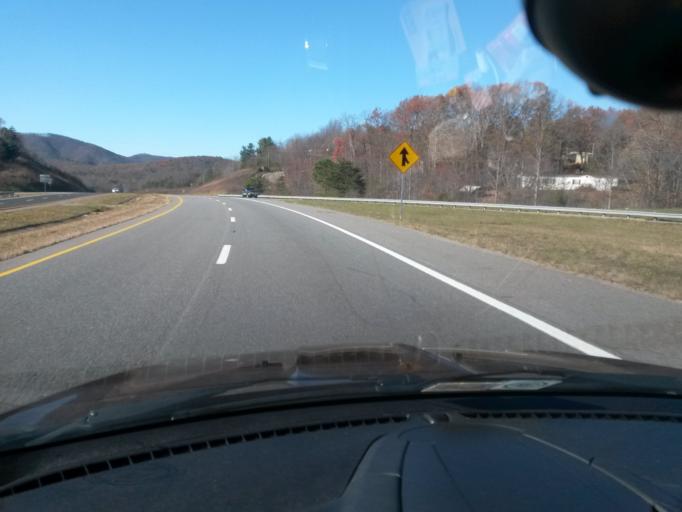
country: US
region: Virginia
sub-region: Patrick County
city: Stuart
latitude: 36.6504
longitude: -80.2717
